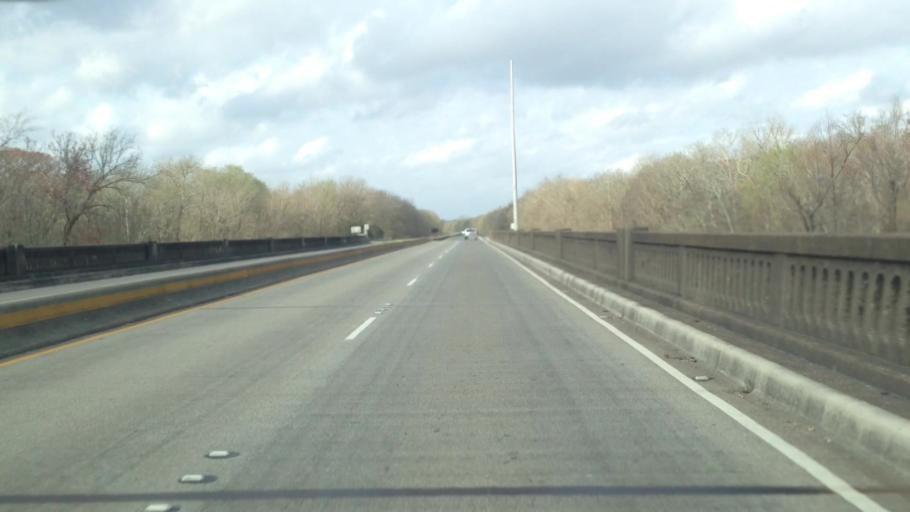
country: US
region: Louisiana
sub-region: Saint Landry Parish
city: Krotz Springs
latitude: 30.5521
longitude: -91.7235
